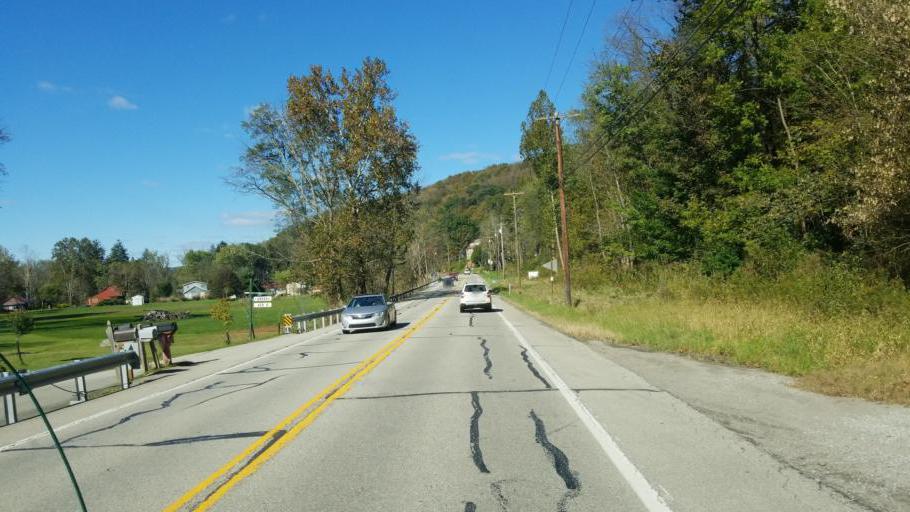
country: US
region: Pennsylvania
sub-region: Westmoreland County
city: Ligonier
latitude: 40.2273
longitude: -79.2201
